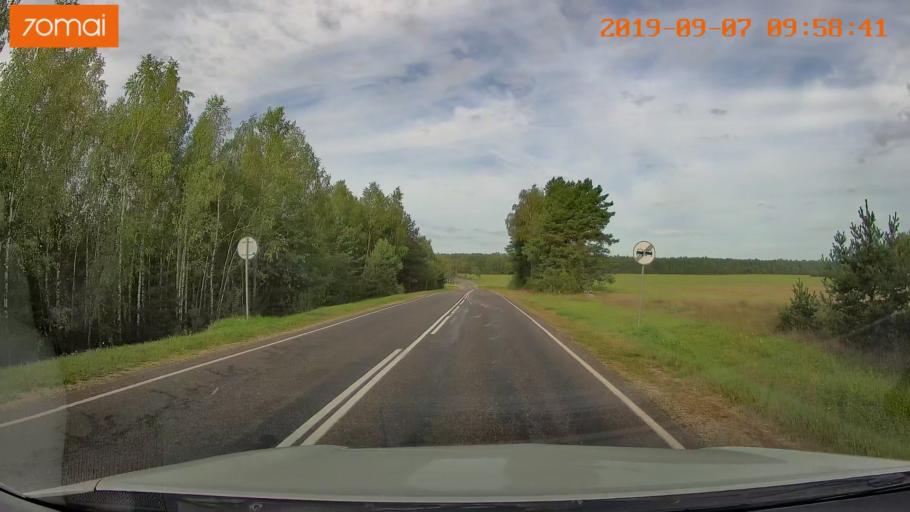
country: BY
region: Grodnenskaya
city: Voranava
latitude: 54.0312
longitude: 25.5302
